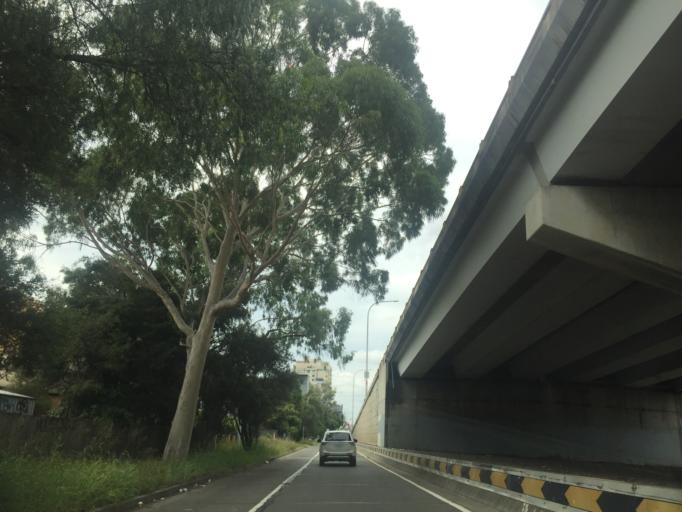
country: AU
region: New South Wales
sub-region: Parramatta
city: Granville
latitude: -33.8281
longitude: 151.0206
